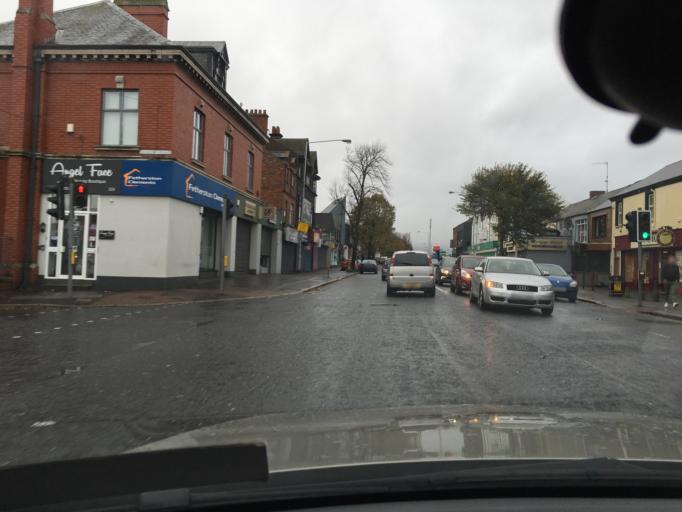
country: GB
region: Northern Ireland
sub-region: Castlereagh District
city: Castlereagh
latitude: 54.5952
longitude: -5.8687
